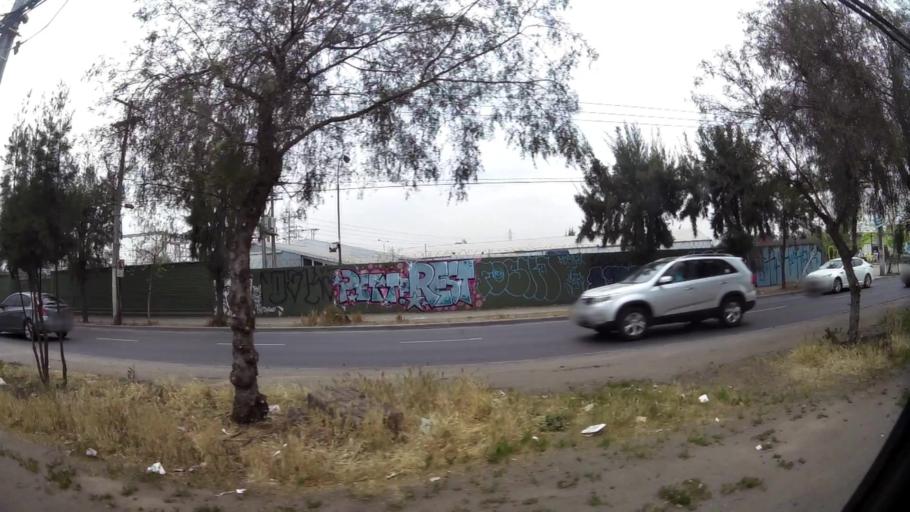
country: CL
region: Santiago Metropolitan
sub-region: Provincia de Santiago
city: Santiago
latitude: -33.4787
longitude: -70.6685
